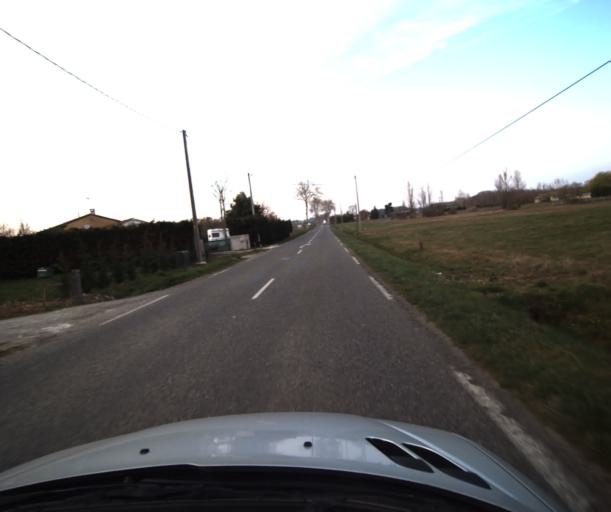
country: FR
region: Midi-Pyrenees
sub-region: Departement de la Haute-Garonne
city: Fronton
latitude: 43.8712
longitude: 1.3800
